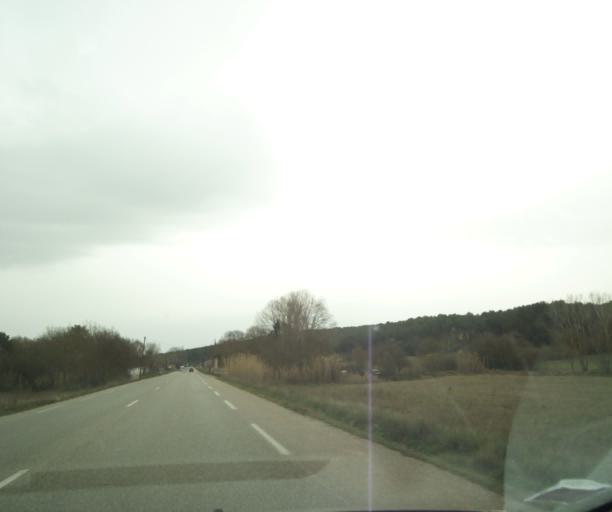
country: FR
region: Provence-Alpes-Cote d'Azur
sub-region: Departement des Bouches-du-Rhone
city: Rousset
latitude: 43.4879
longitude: 5.6009
